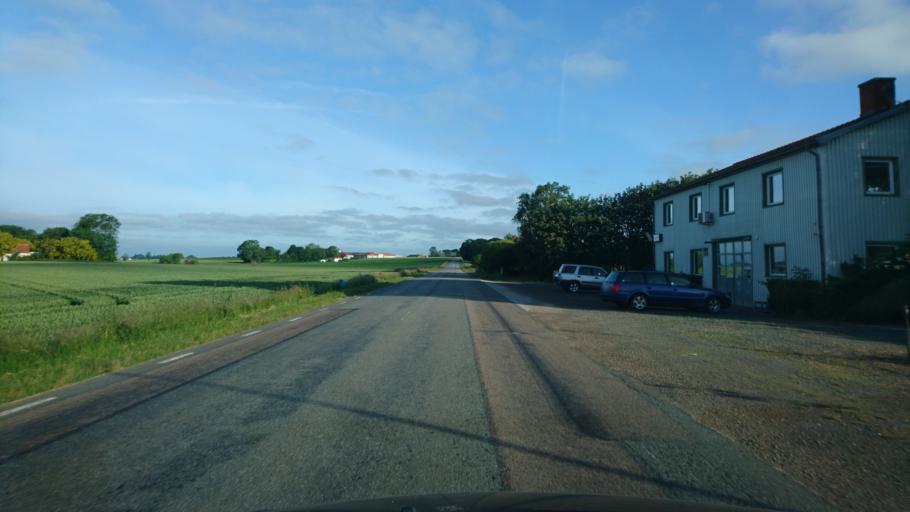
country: SE
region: Skane
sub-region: Tomelilla Kommun
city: Tomelilla
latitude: 55.4599
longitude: 14.1062
